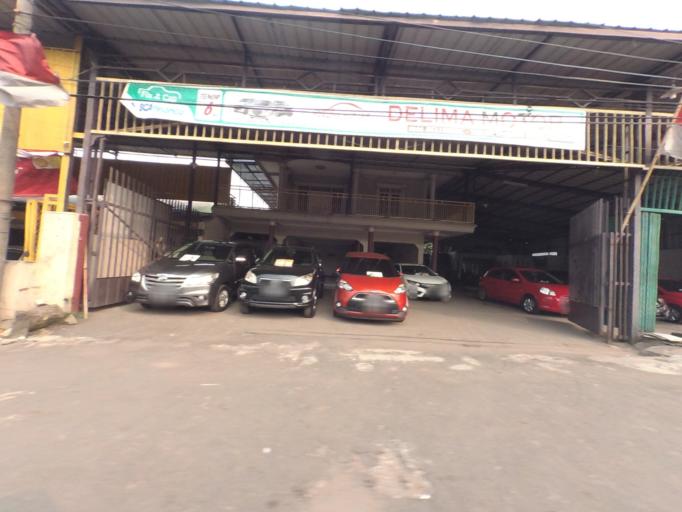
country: ID
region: West Java
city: Ciampea
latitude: -6.5698
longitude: 106.6684
